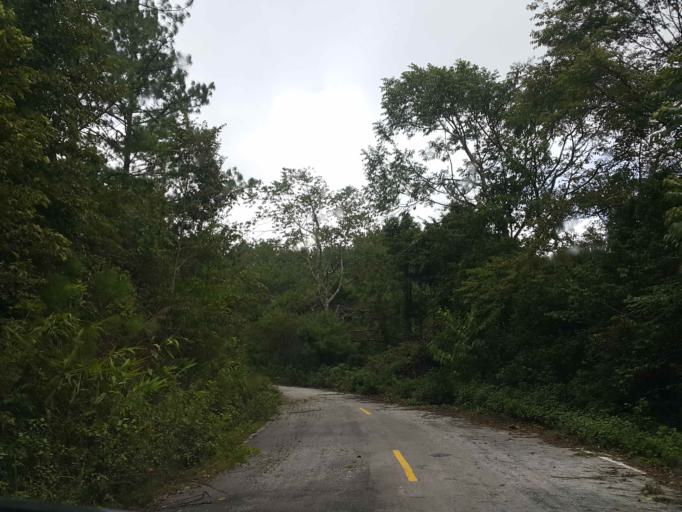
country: TH
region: Chiang Mai
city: Chom Thong
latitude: 18.5117
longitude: 98.5342
